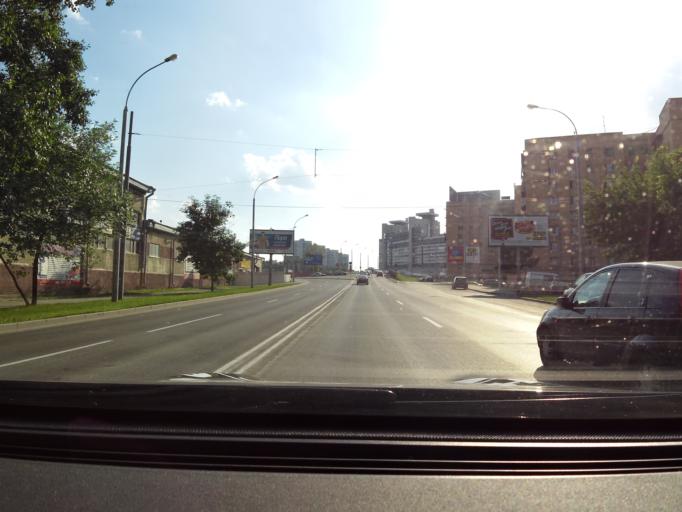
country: RU
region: Sverdlovsk
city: Yekaterinburg
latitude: 56.8277
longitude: 60.5659
